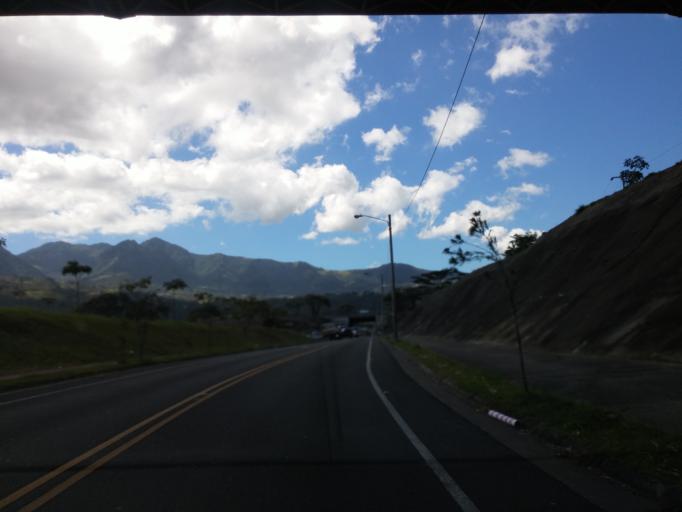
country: CR
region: San Jose
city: San Felipe
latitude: 9.9238
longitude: -84.1057
